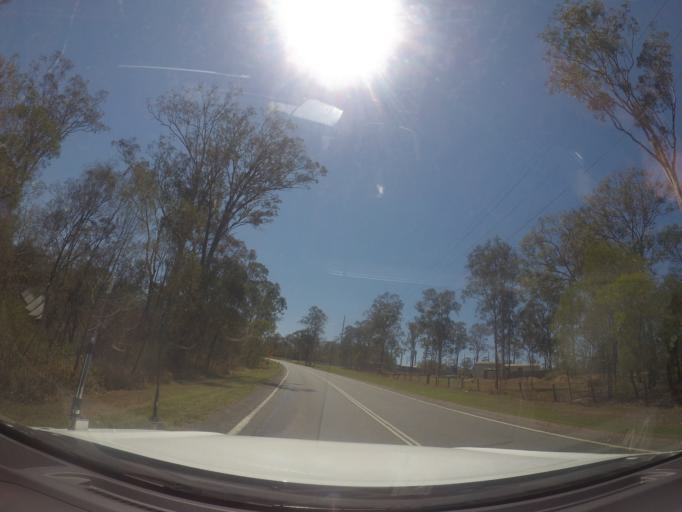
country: AU
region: Queensland
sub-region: Logan
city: North Maclean
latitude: -27.8097
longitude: 153.0424
